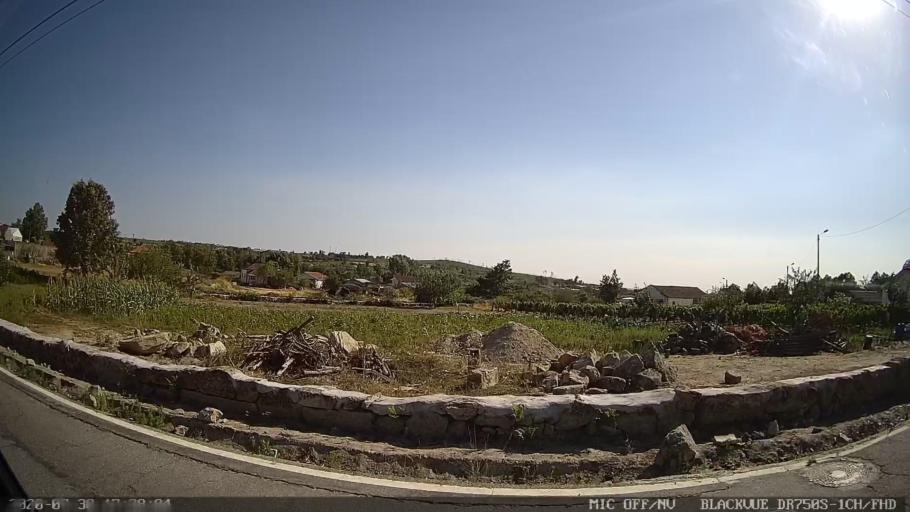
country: PT
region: Vila Real
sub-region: Murca
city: Murca
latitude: 41.3266
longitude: -7.4646
